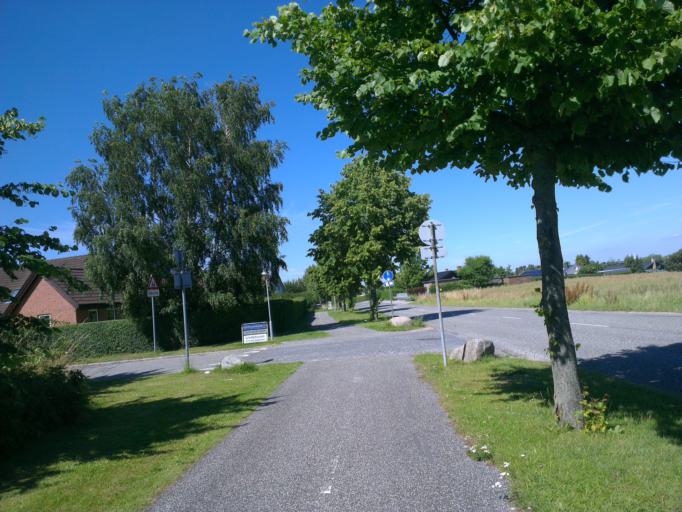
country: DK
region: Capital Region
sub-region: Frederikssund Kommune
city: Slangerup
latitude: 55.8381
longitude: 12.1786
